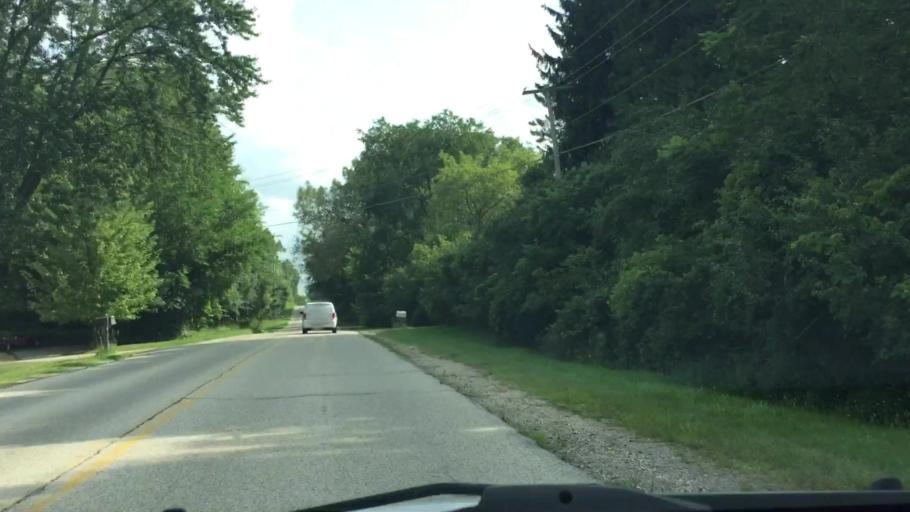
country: US
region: Wisconsin
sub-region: Waukesha County
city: Wales
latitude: 43.0467
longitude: -88.3496
